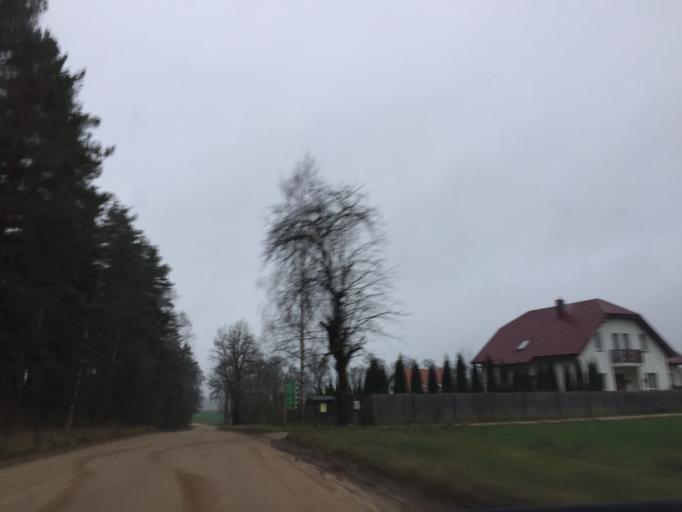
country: LV
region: Koceni
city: Koceni
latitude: 57.5381
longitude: 25.3330
